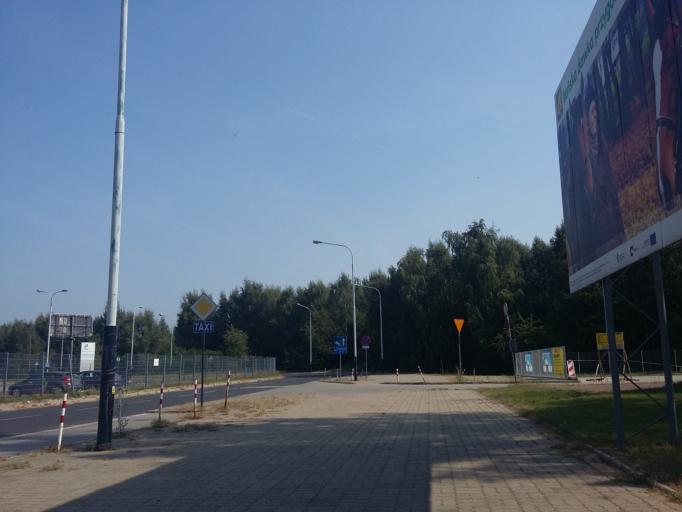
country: PL
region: Lodz Voivodeship
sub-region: Powiat pabianicki
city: Ksawerow
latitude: 51.7279
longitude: 19.4039
